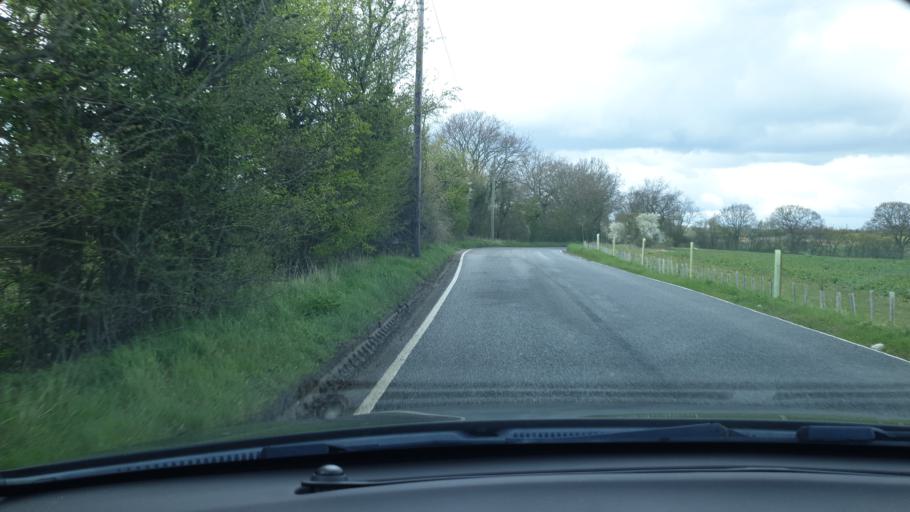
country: GB
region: England
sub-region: Essex
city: Little Clacton
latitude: 51.9061
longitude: 1.1748
